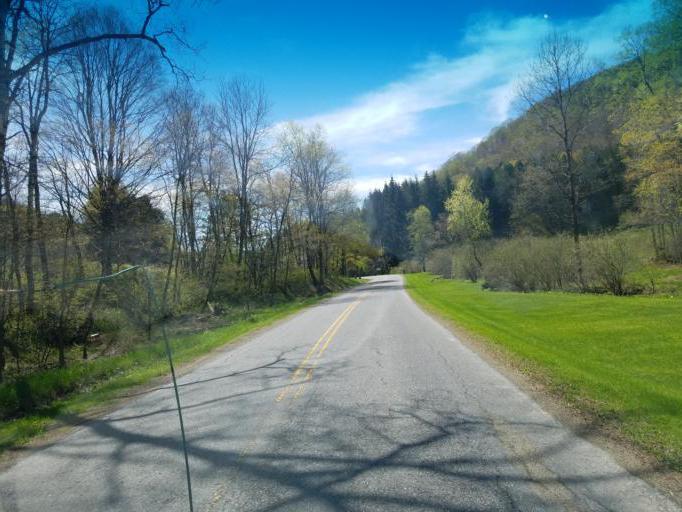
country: US
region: Pennsylvania
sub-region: Potter County
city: Galeton
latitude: 41.8724
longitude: -77.7259
